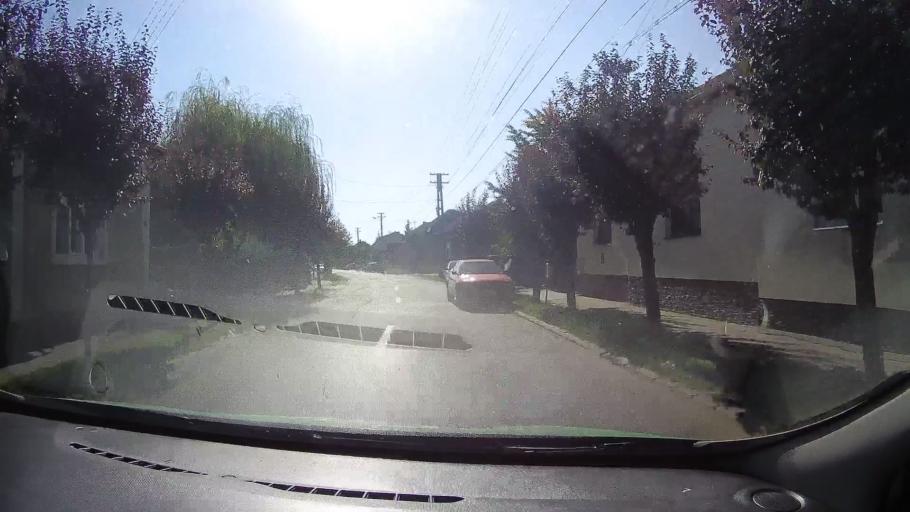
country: RO
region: Satu Mare
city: Carei
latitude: 47.6913
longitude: 22.4705
